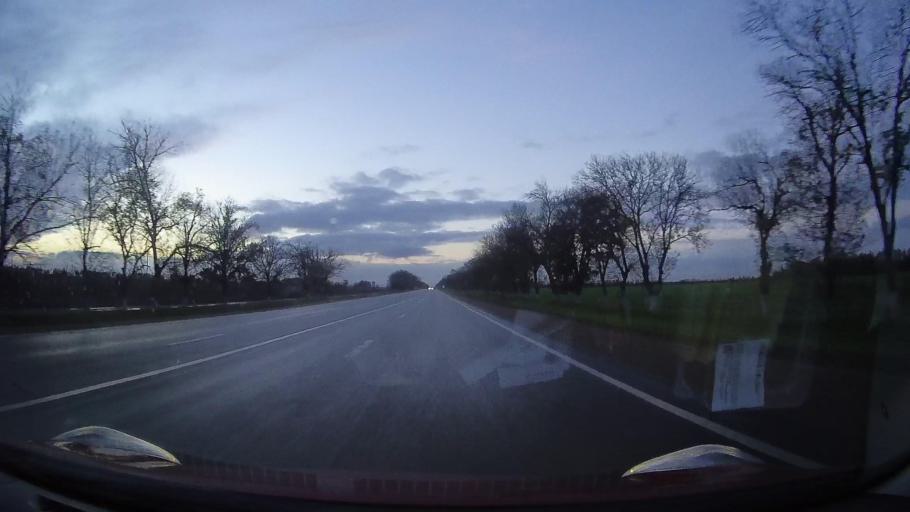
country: RU
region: Krasnodarskiy
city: Zavetnyy
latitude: 44.8843
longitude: 41.2208
